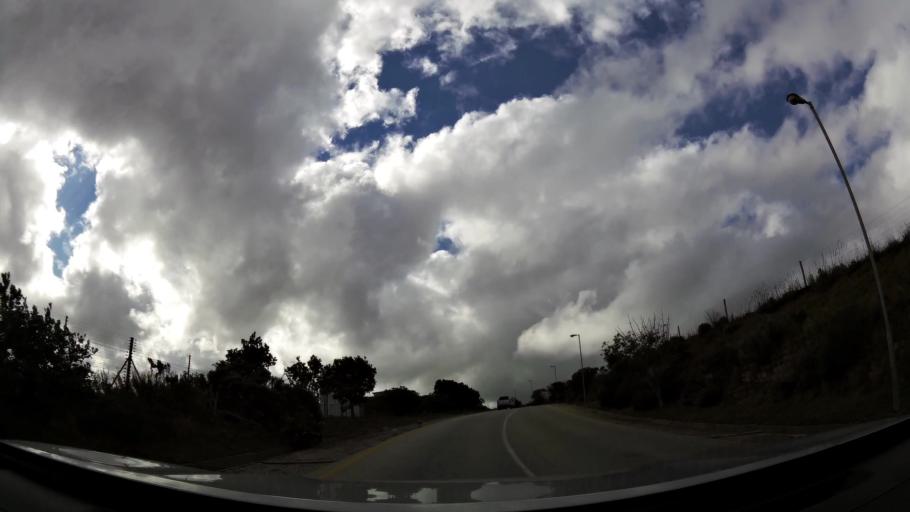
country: ZA
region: Western Cape
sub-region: Eden District Municipality
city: Knysna
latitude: -34.0731
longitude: 23.0857
